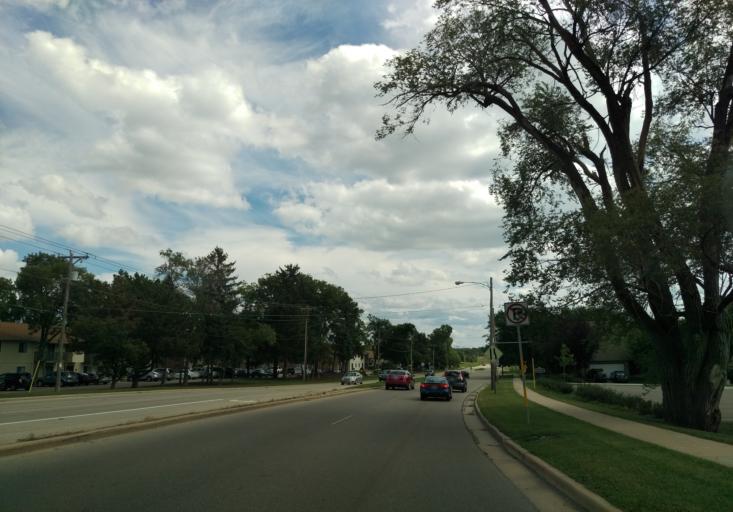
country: US
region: Wisconsin
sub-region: Dane County
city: Middleton
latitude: 43.1118
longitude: -89.4712
